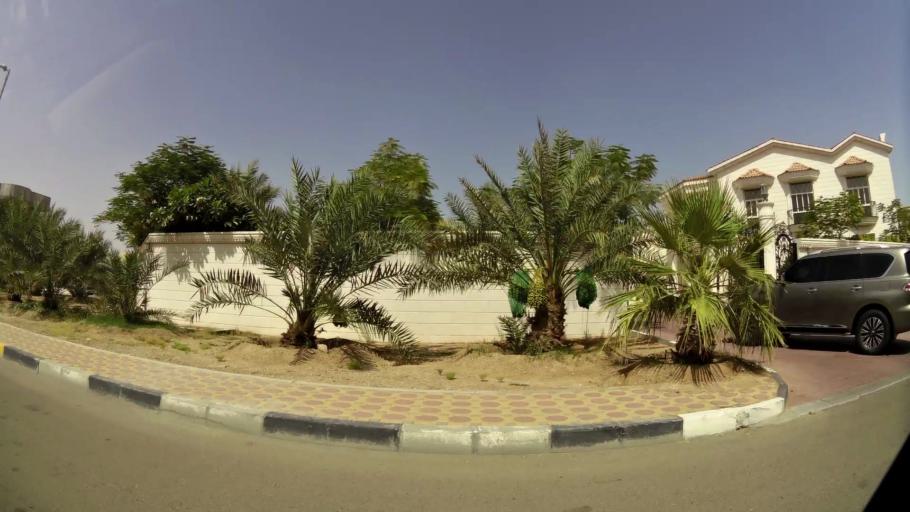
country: AE
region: Abu Dhabi
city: Al Ain
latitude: 24.2253
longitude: 55.6882
